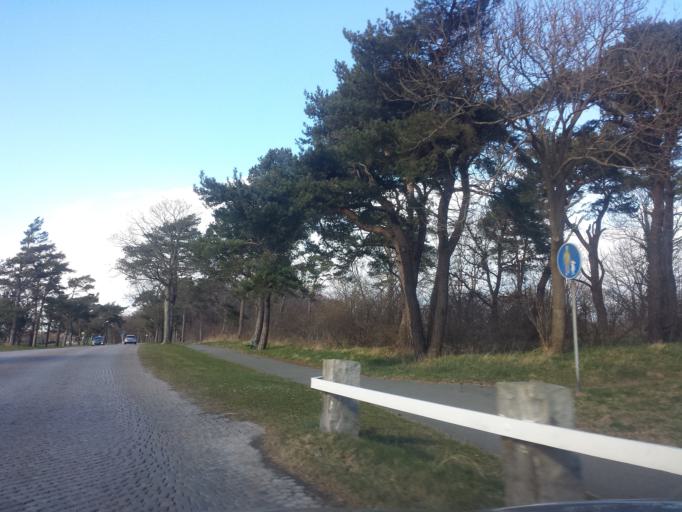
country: SE
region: Skane
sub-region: Simrishamns Kommun
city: Simrishamn
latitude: 55.5635
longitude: 14.3369
